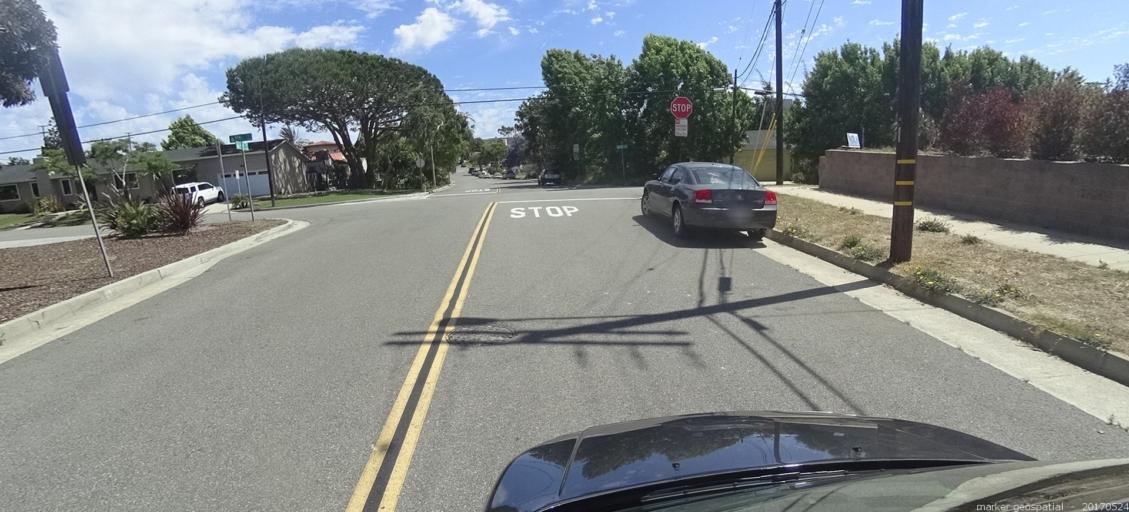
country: US
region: California
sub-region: Los Angeles County
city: Redondo Beach
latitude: 33.8372
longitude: -118.3779
